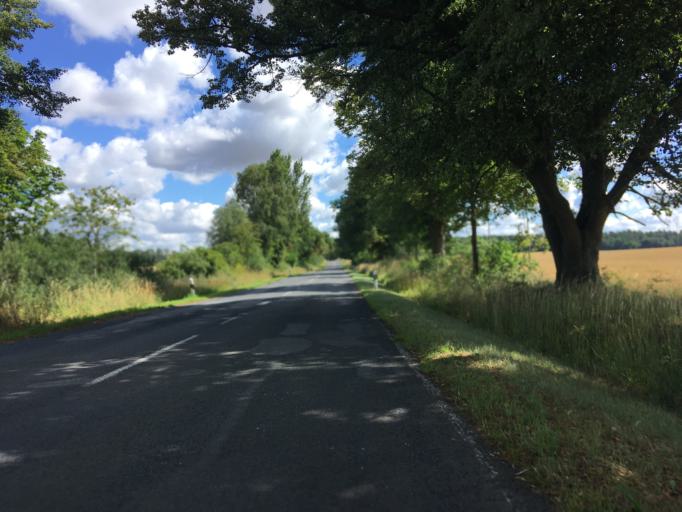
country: DE
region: Brandenburg
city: Mittenwalde
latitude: 53.1847
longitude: 13.5848
